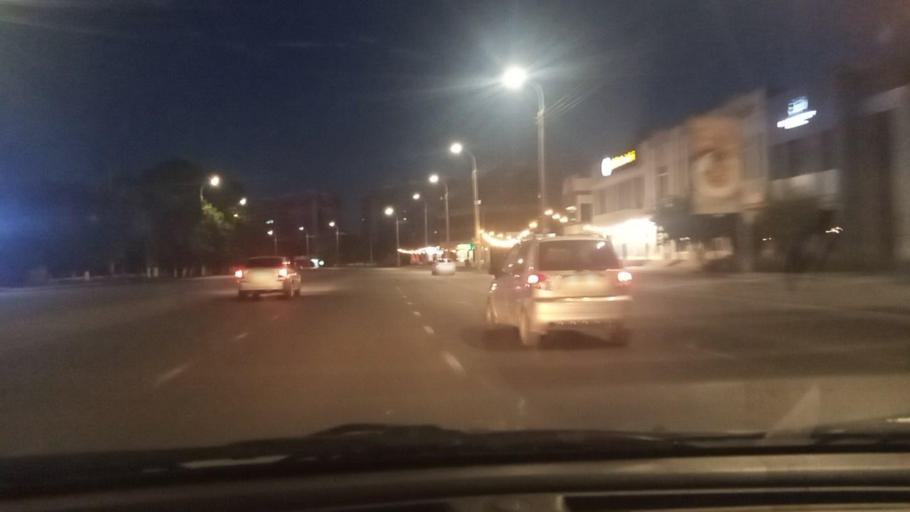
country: UZ
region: Toshkent Shahri
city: Tashkent
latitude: 41.2693
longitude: 69.2583
